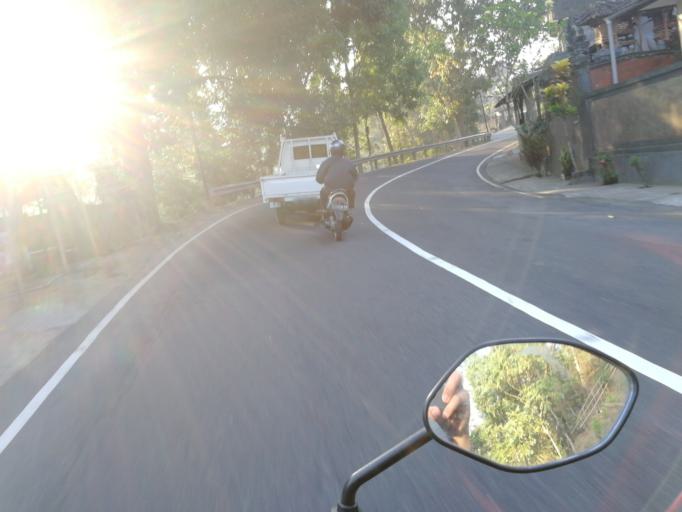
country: ID
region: Bali
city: Tistagede
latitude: -8.3774
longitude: 115.6082
